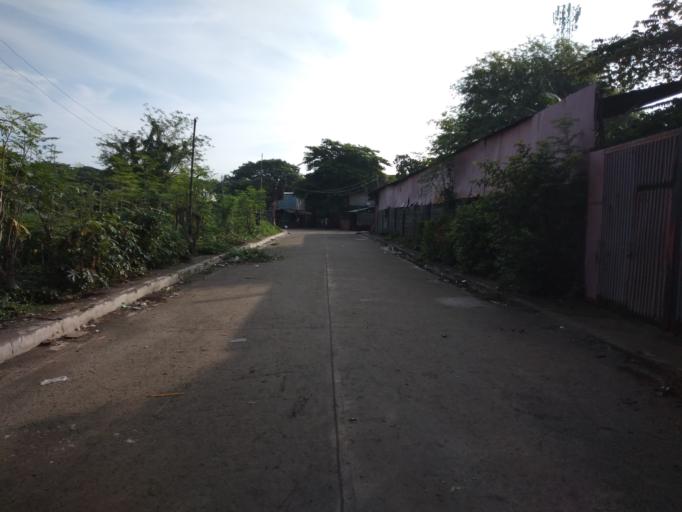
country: PH
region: Calabarzon
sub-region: Province of Rizal
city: Taytay
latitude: 14.5546
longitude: 121.1222
